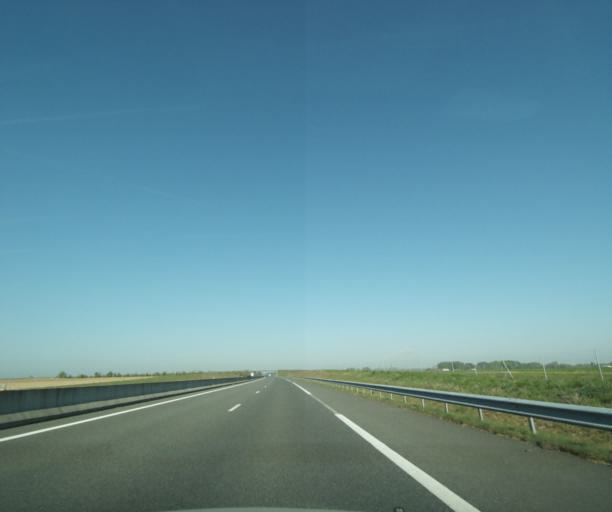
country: FR
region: Centre
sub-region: Departement du Loiret
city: Pannes
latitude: 48.0779
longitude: 2.6251
